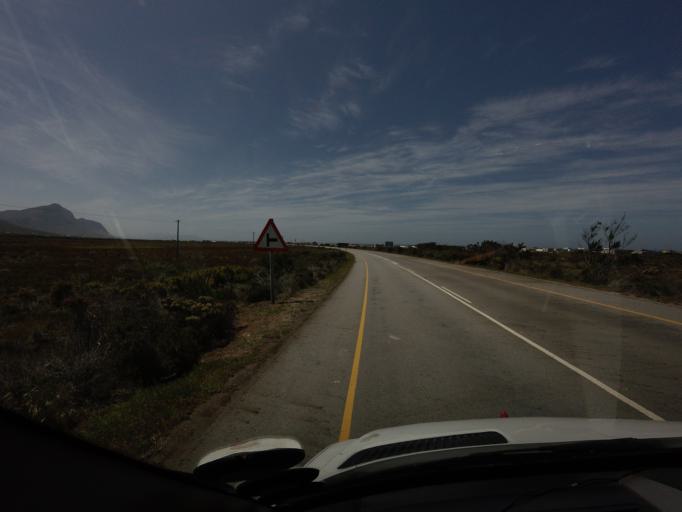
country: ZA
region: Western Cape
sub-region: Overberg District Municipality
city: Grabouw
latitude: -34.3599
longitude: 18.8645
